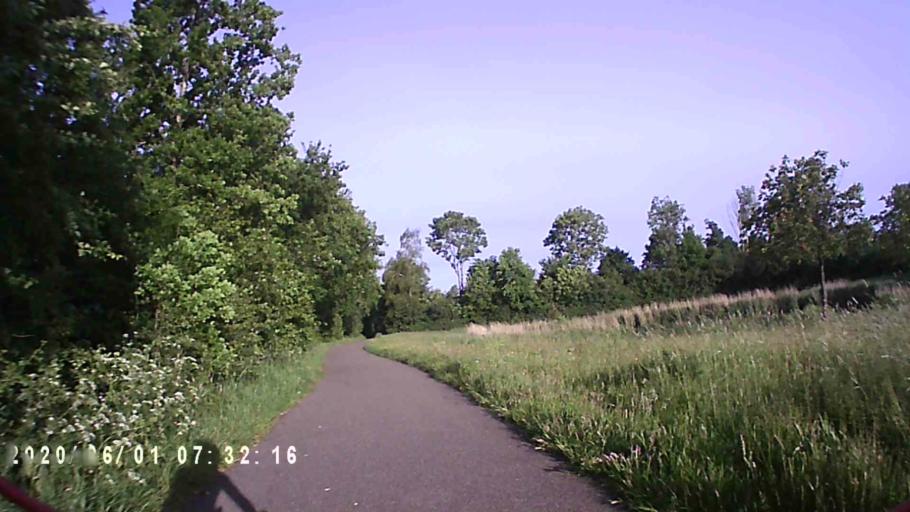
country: NL
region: Friesland
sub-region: Gemeente Dongeradeel
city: Dokkum
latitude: 53.3118
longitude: 5.9979
